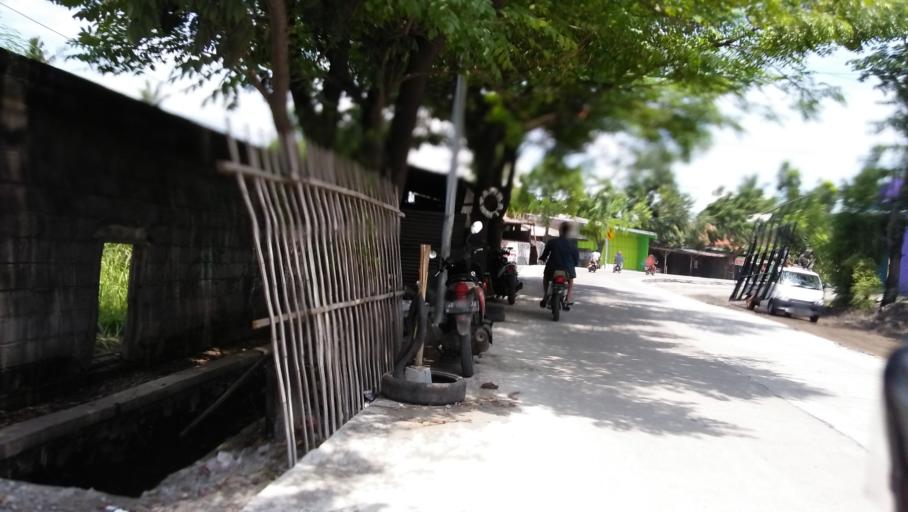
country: ID
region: Central Java
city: Mranggen
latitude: -6.9820
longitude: 110.4789
